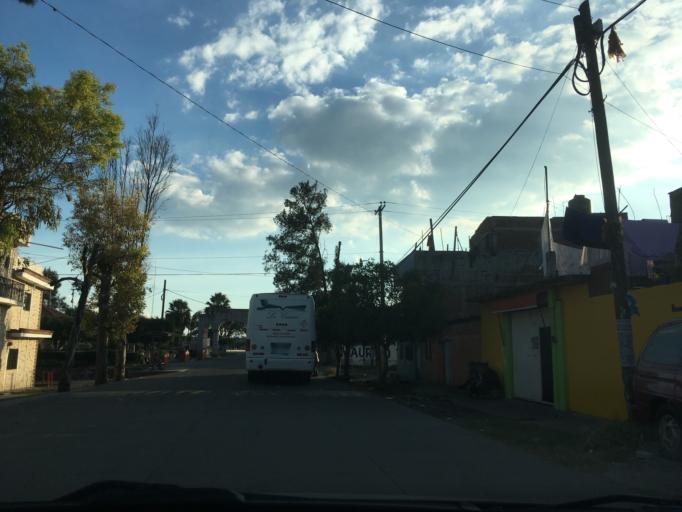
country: MX
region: Michoacan
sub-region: Cuitzeo
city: San Juan Benito Juarez (San Juan Tararameo)
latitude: 19.8679
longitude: -101.1427
